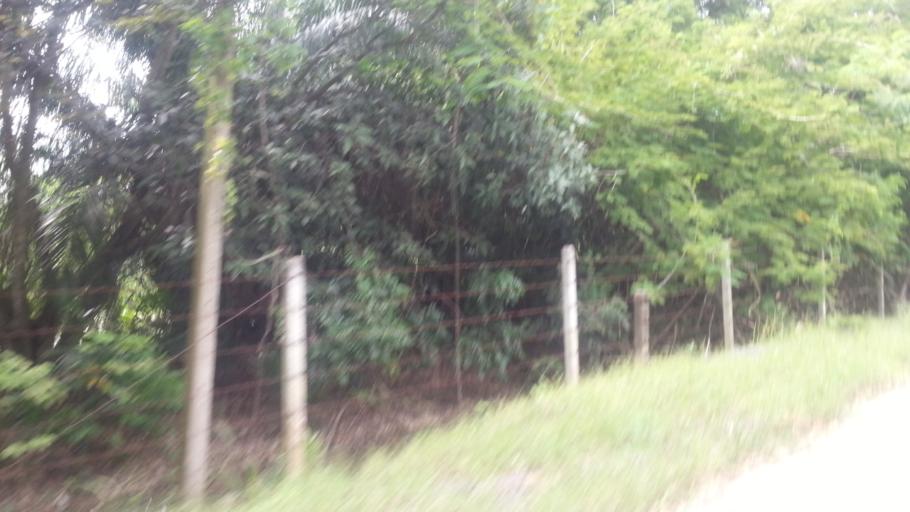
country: TH
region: Pathum Thani
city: Nong Suea
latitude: 14.1074
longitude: 100.8236
